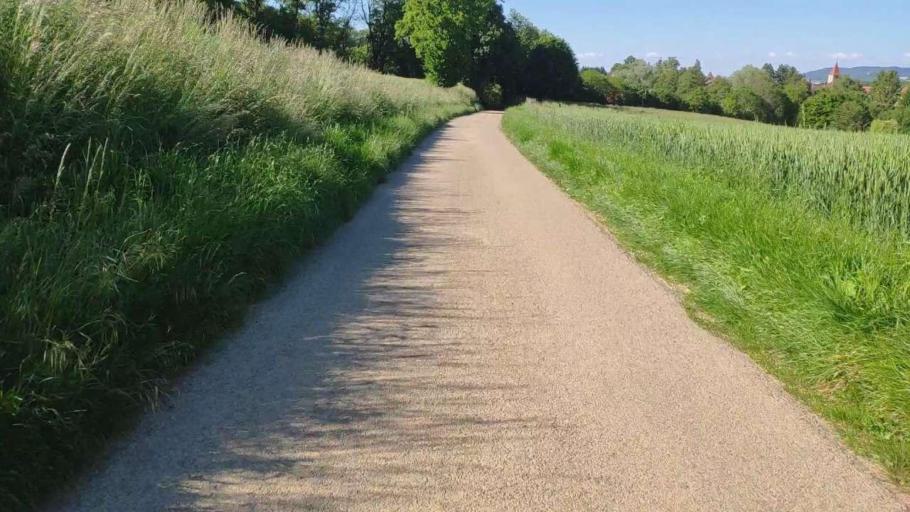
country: FR
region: Franche-Comte
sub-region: Departement du Jura
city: Montmorot
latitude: 46.7262
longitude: 5.5517
